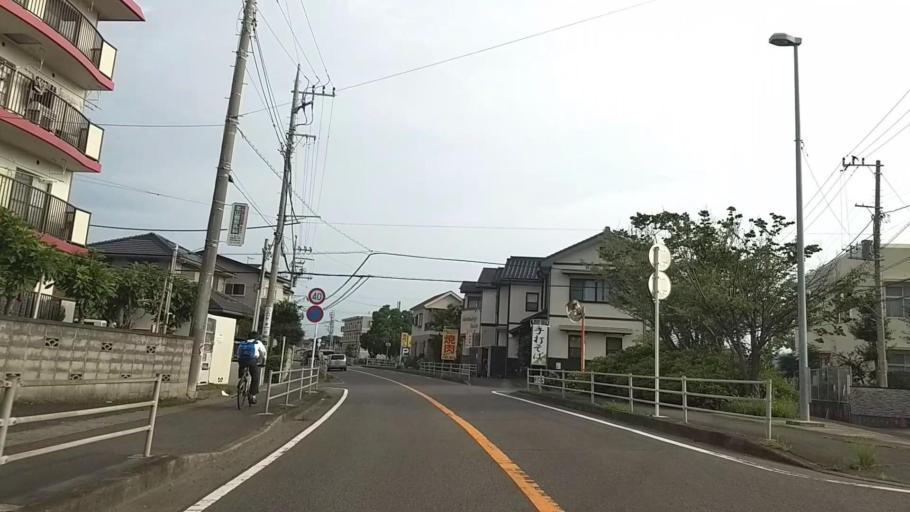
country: JP
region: Kanagawa
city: Hiratsuka
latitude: 35.3378
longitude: 139.3100
